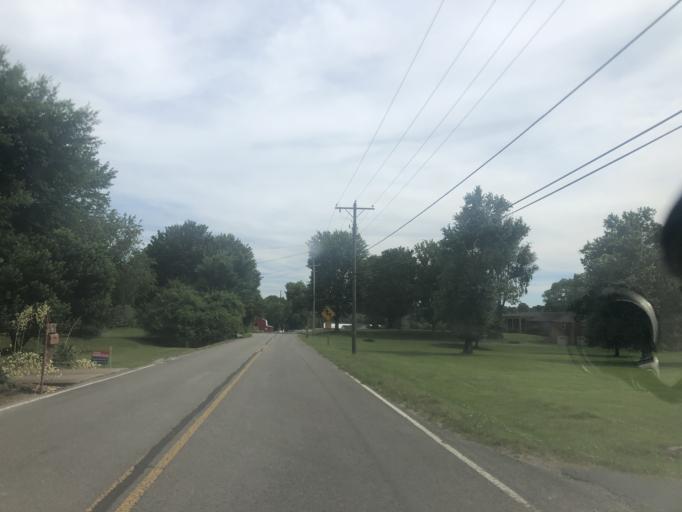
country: US
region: Tennessee
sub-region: Davidson County
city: Lakewood
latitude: 36.2014
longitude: -86.6647
